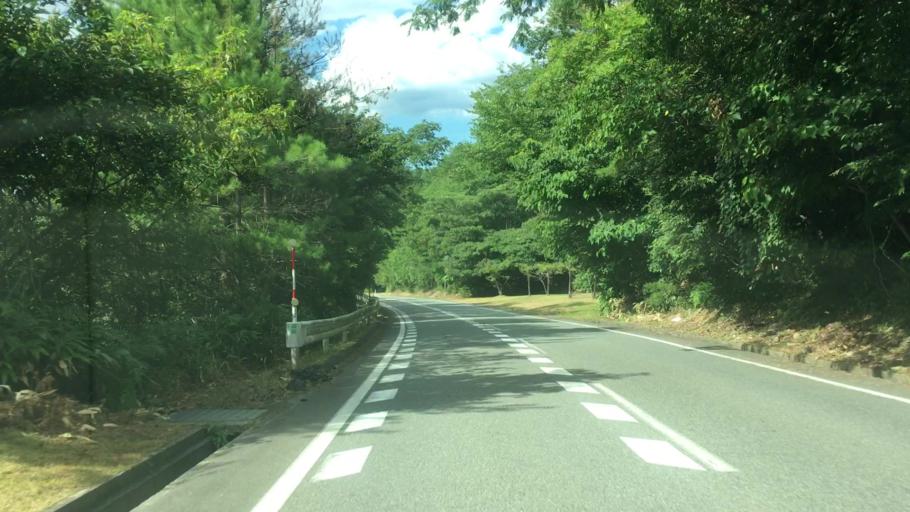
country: JP
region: Hyogo
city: Toyooka
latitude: 35.5211
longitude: 134.7913
